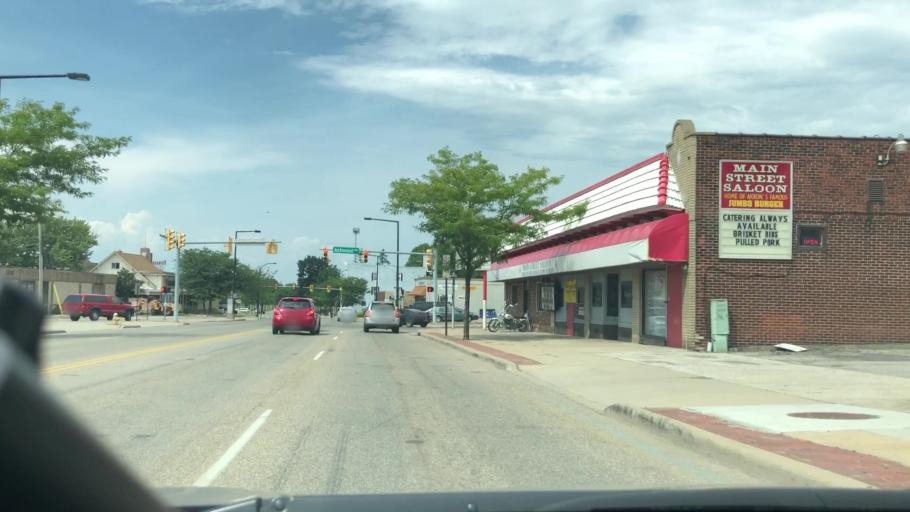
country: US
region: Ohio
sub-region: Summit County
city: Akron
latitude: 41.0462
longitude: -81.5274
